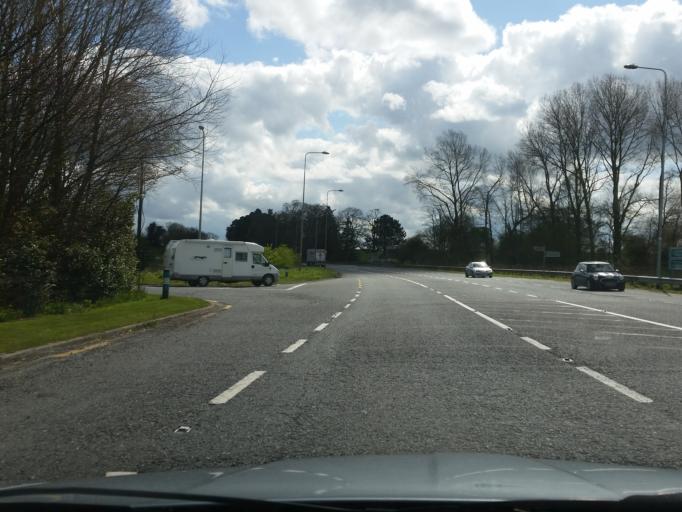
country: IE
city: Kentstown
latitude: 53.6231
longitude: -6.4878
